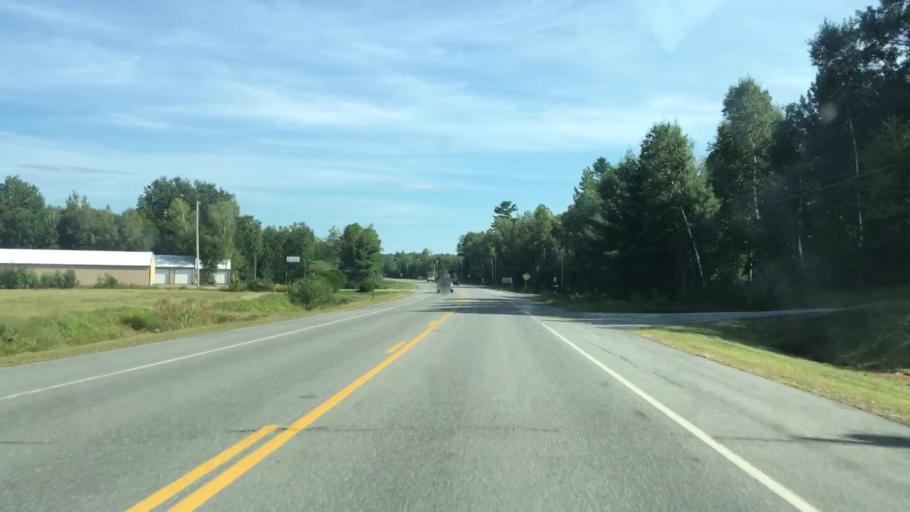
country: US
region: Maine
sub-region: Penobscot County
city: Lincoln
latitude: 45.3606
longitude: -68.5457
